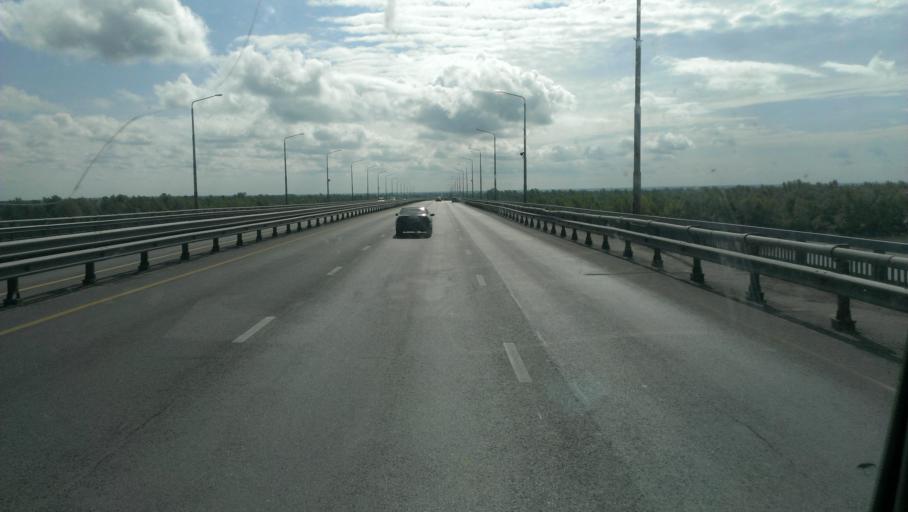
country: RU
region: Altai Krai
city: Zaton
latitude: 53.3236
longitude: 83.8030
